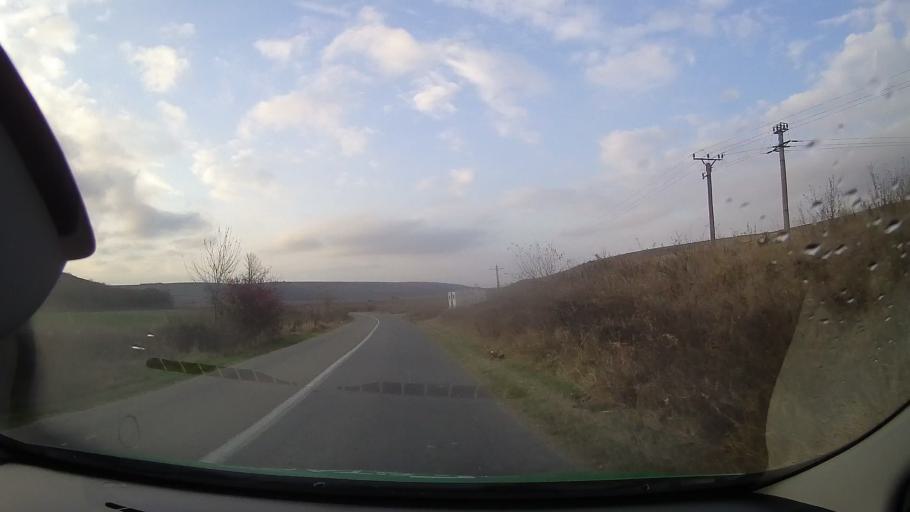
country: RO
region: Constanta
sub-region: Comuna Dobromir
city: Dobromir
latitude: 44.0341
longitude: 27.8539
